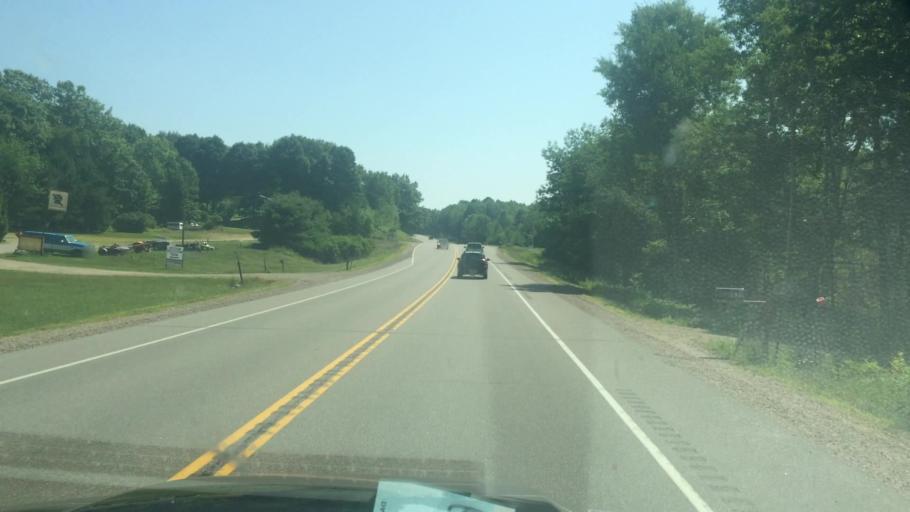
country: US
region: Wisconsin
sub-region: Oneida County
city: Rhinelander
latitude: 45.6163
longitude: -89.5080
